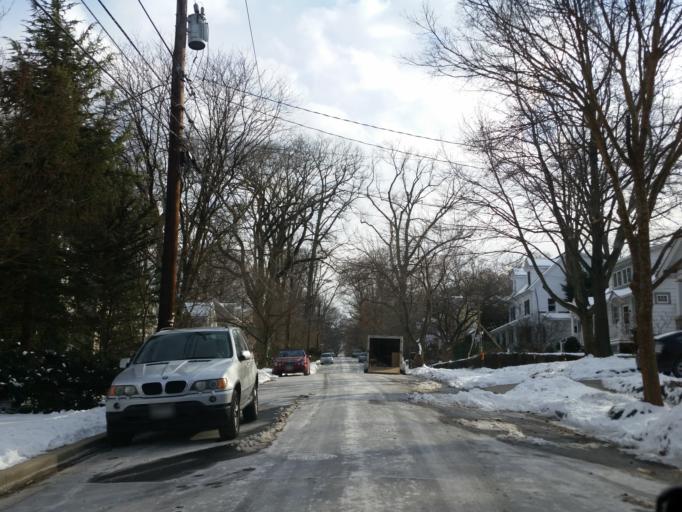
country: US
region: Maryland
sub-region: Montgomery County
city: Chevy Chase
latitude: 38.9840
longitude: -77.0833
